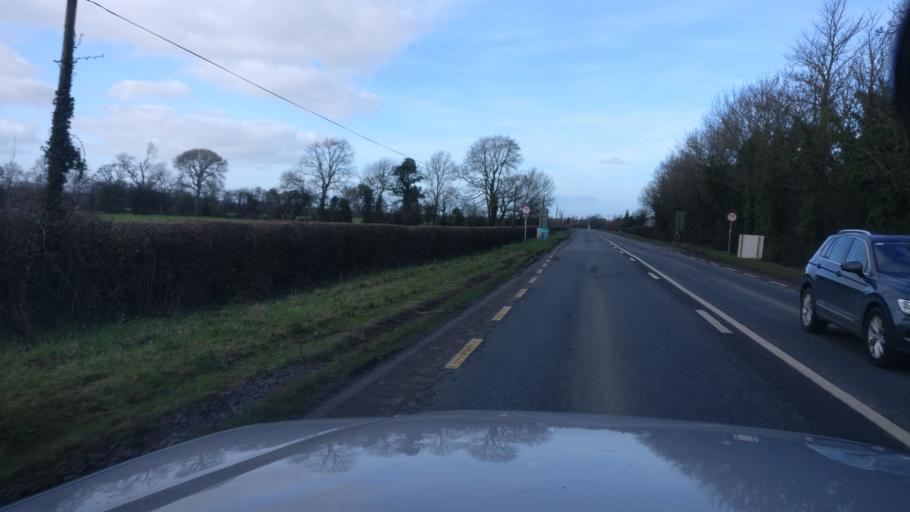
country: IE
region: Leinster
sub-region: Laois
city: Portlaoise
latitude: 53.0558
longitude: -7.3230
